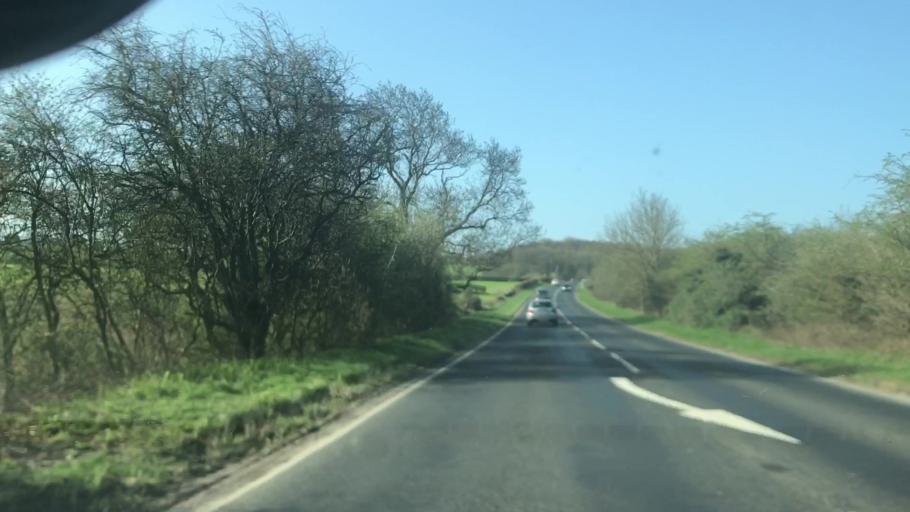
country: GB
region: England
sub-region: City and Borough of Leeds
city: Shadwell
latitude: 53.8720
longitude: -1.5168
